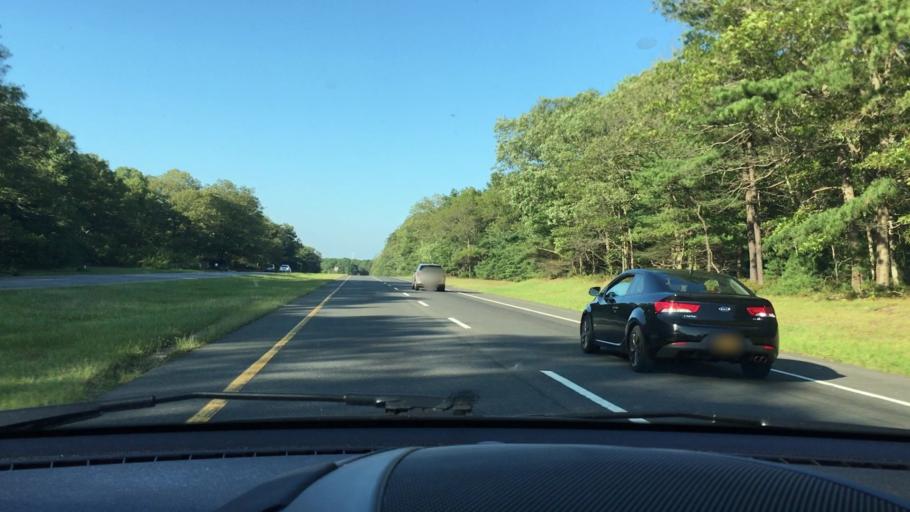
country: US
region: New York
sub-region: Suffolk County
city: Ridge
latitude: 40.8827
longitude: -72.8892
